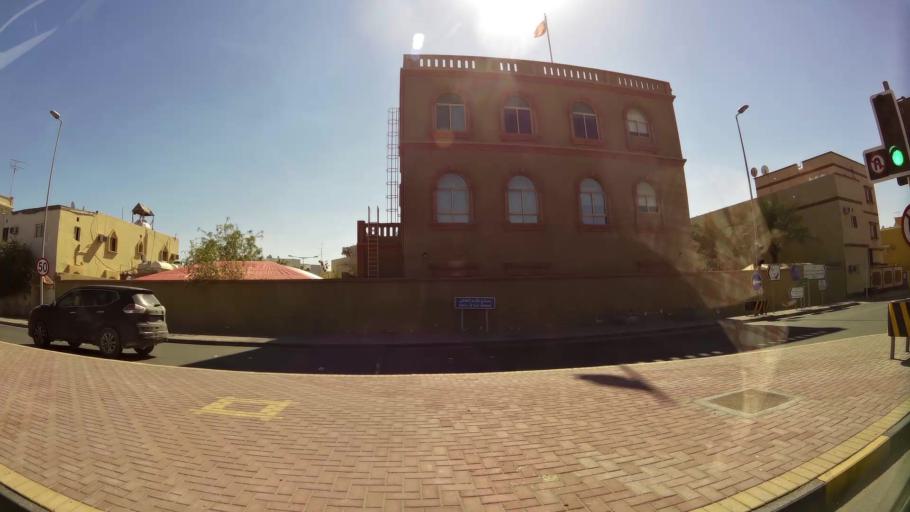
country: BH
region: Muharraq
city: Al Hadd
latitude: 26.2557
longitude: 50.6484
